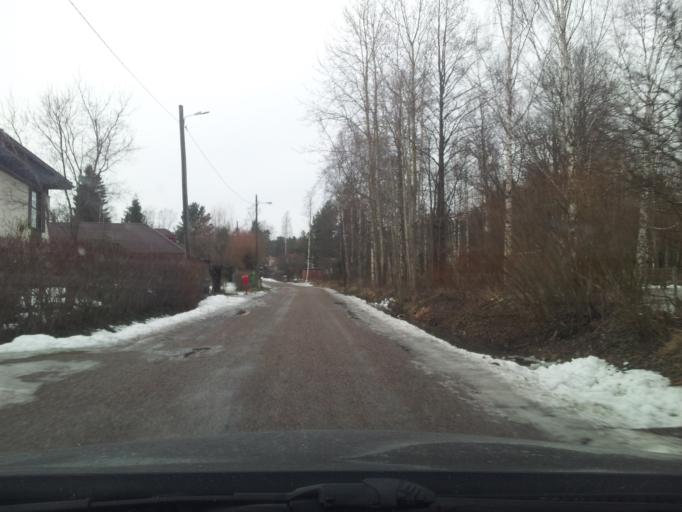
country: FI
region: Uusimaa
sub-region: Helsinki
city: Koukkuniemi
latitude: 60.1668
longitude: 24.7251
